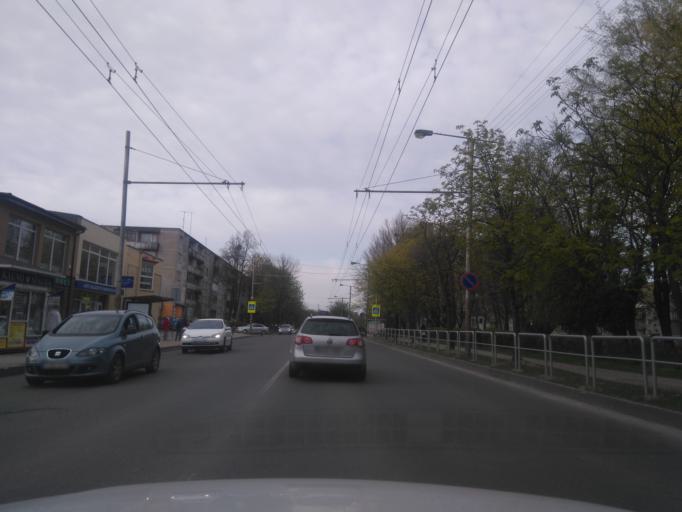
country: LT
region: Kauno apskritis
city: Dainava (Kaunas)
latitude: 54.9093
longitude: 23.9738
